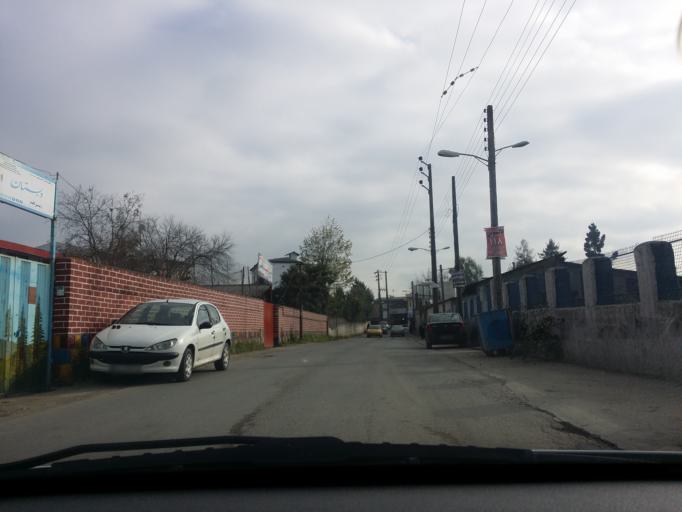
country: IR
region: Mazandaran
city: Chalus
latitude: 36.6590
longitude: 51.4040
